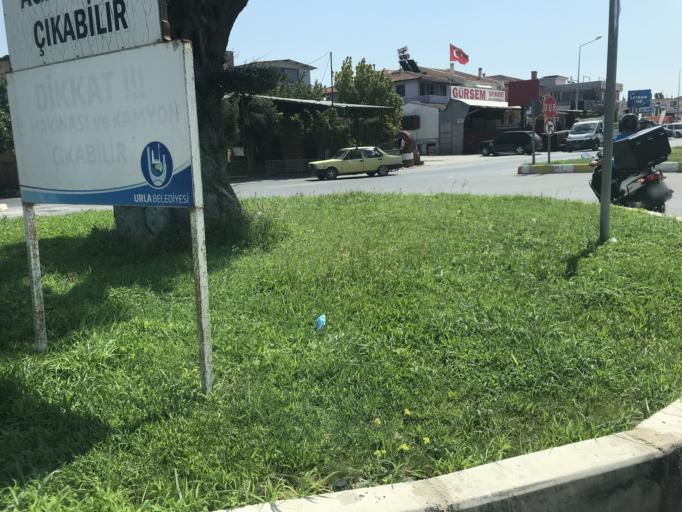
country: TR
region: Izmir
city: Urla
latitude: 38.3239
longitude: 26.7508
